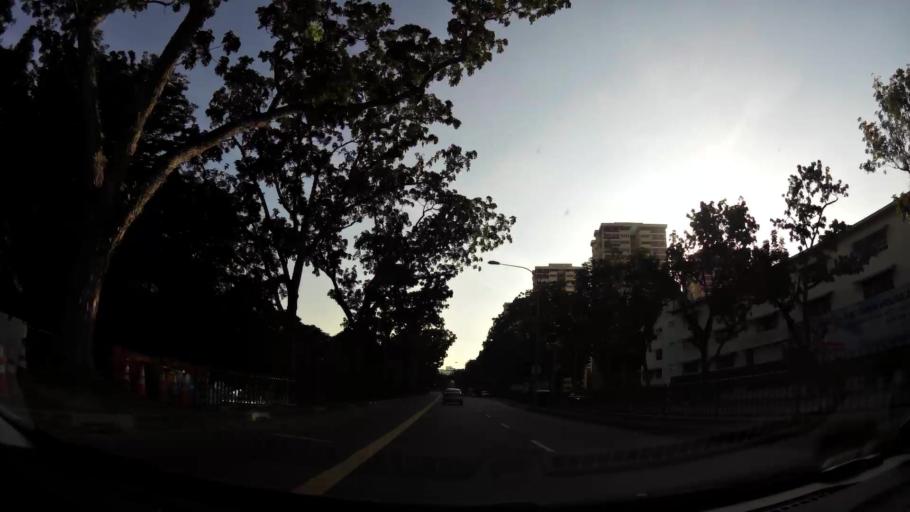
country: SG
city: Singapore
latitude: 1.3076
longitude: 103.9198
